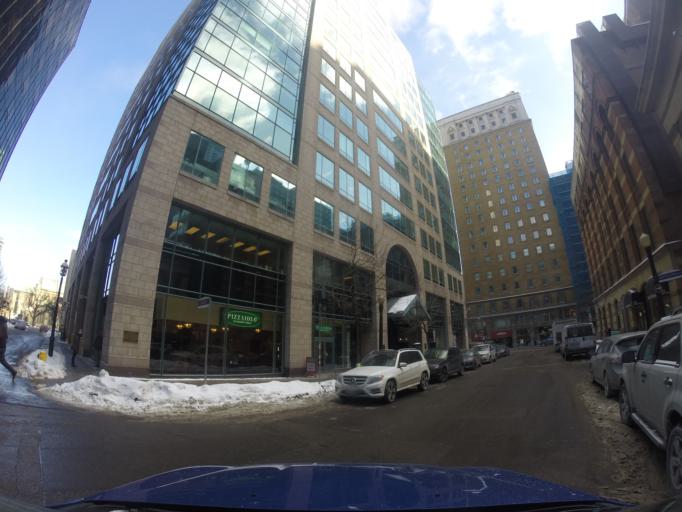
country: CA
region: Ontario
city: Toronto
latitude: 43.6501
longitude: -79.3764
